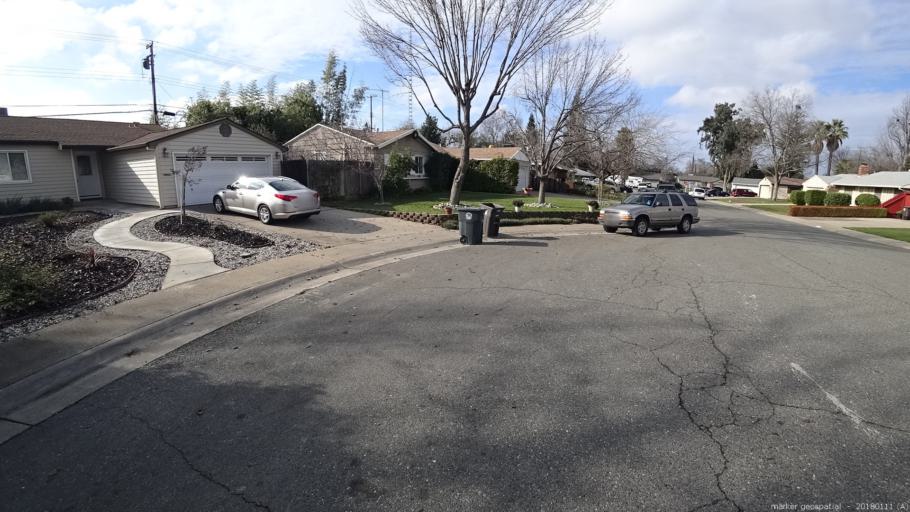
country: US
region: California
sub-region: Sacramento County
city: Rancho Cordova
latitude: 38.6098
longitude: -121.2954
